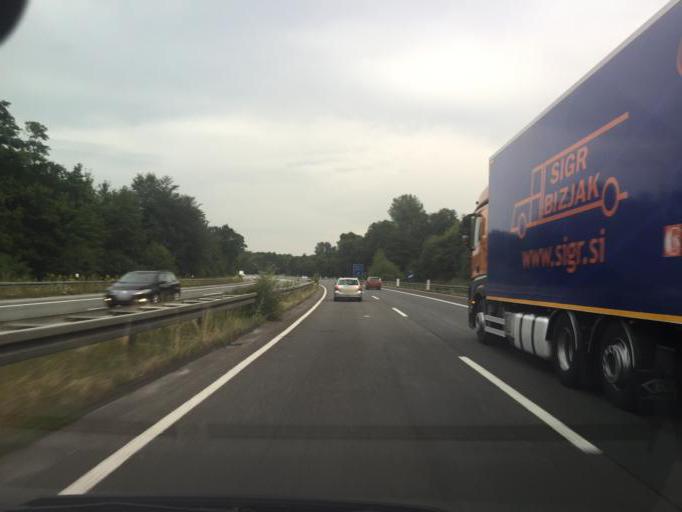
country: DE
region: North Rhine-Westphalia
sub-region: Regierungsbezirk Dusseldorf
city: Nettetal
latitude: 51.2878
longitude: 6.2677
